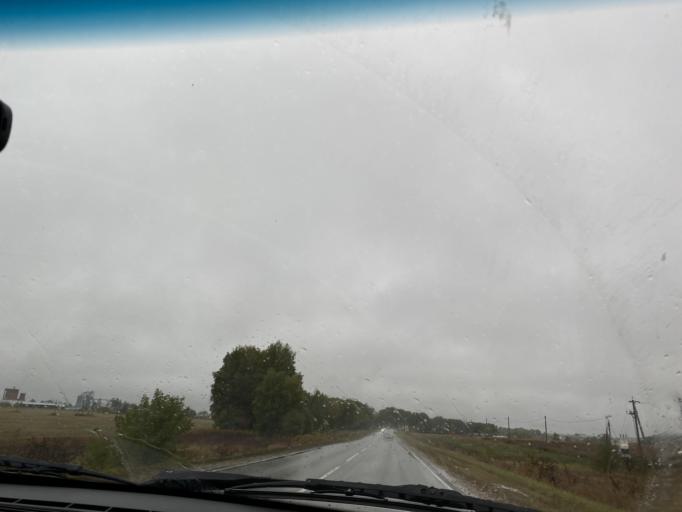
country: RU
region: Rjazan
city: Murmino
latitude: 54.4609
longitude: 39.8755
